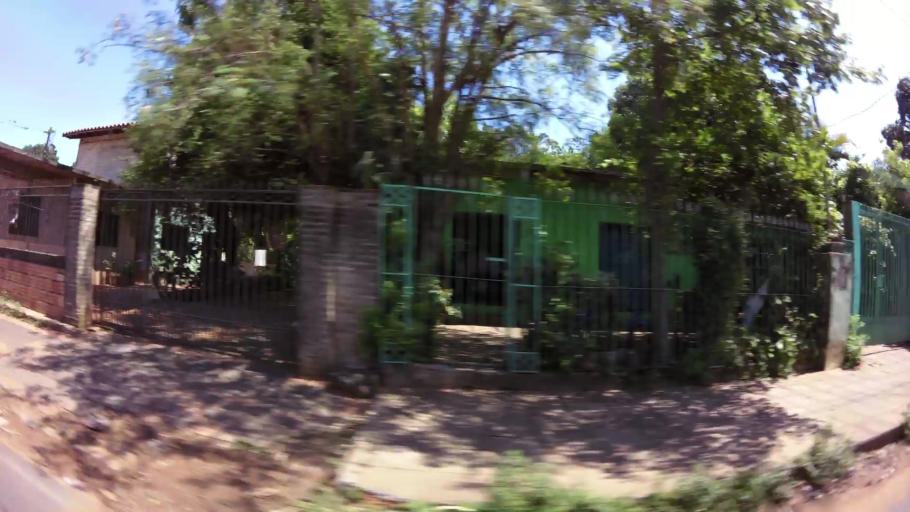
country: PY
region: Central
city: Nemby
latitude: -25.3901
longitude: -57.5258
